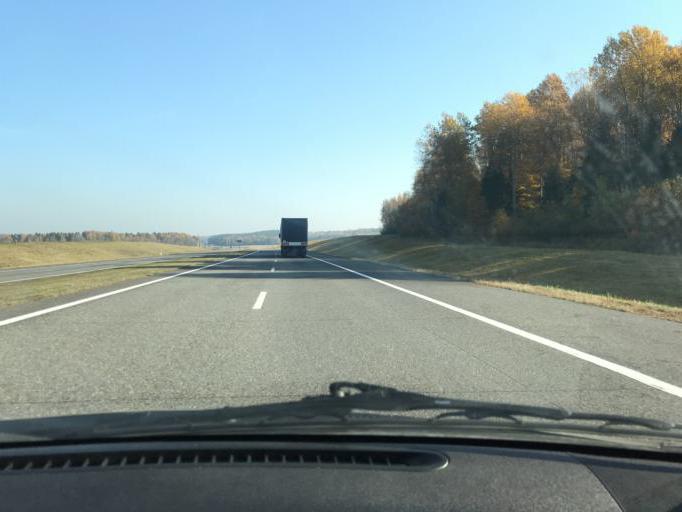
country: BY
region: Vitebsk
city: Talachyn
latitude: 54.4086
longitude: 29.4946
